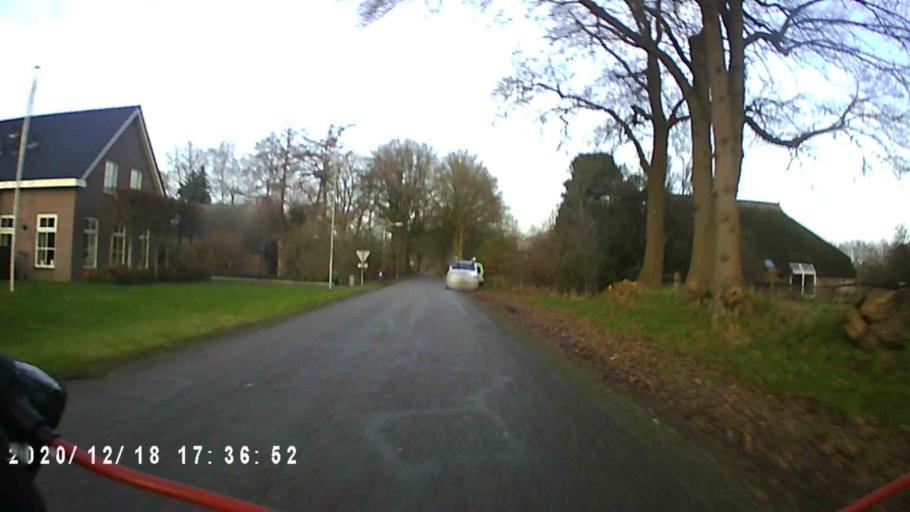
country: NL
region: Drenthe
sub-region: Gemeente Tynaarlo
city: Vries
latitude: 53.0830
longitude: 6.5741
